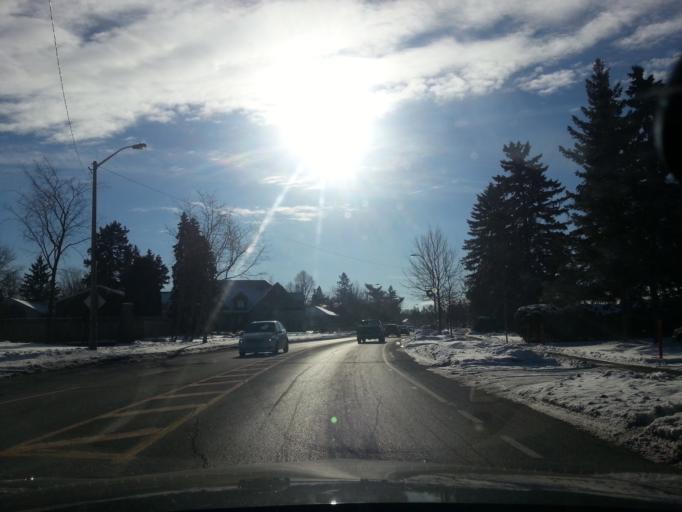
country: CA
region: Ontario
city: Ottawa
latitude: 45.3977
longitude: -75.6617
